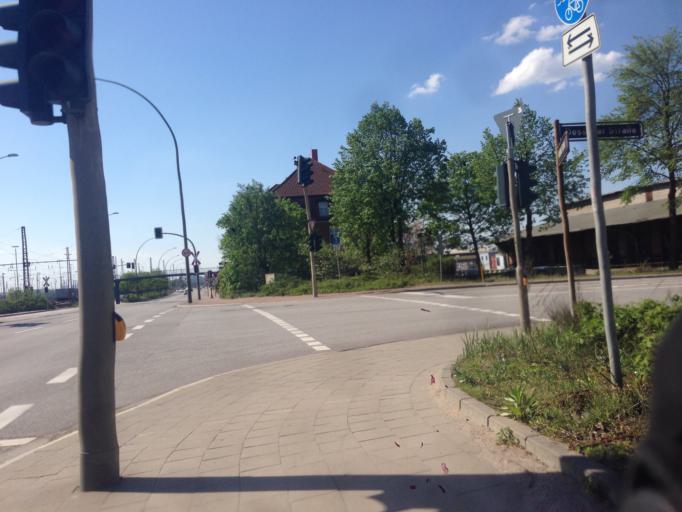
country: DE
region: Hamburg
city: Kleiner Grasbrook
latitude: 53.5234
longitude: 10.0085
